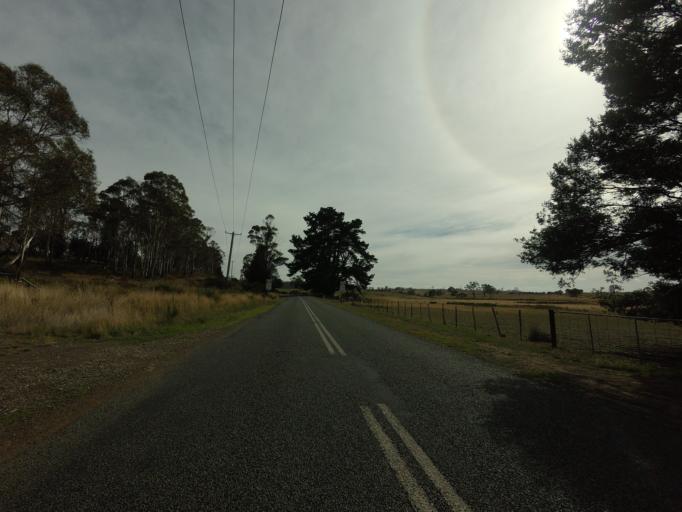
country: AU
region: Tasmania
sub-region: Brighton
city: Bridgewater
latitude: -42.3462
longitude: 147.4044
